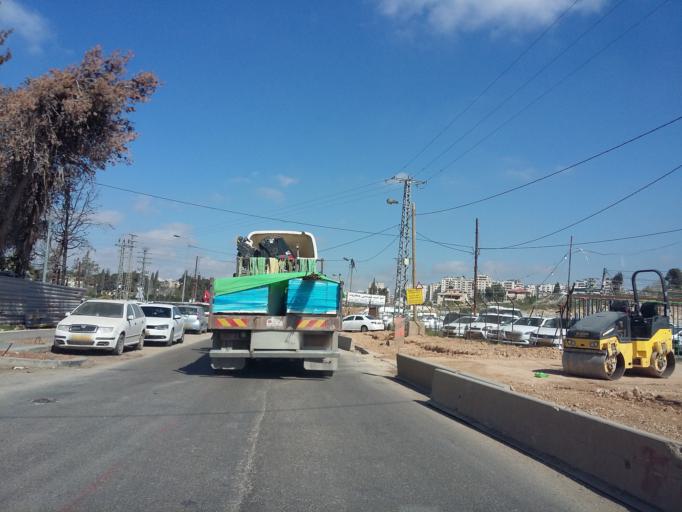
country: PS
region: West Bank
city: Qalandiya
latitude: 31.8589
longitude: 35.2220
